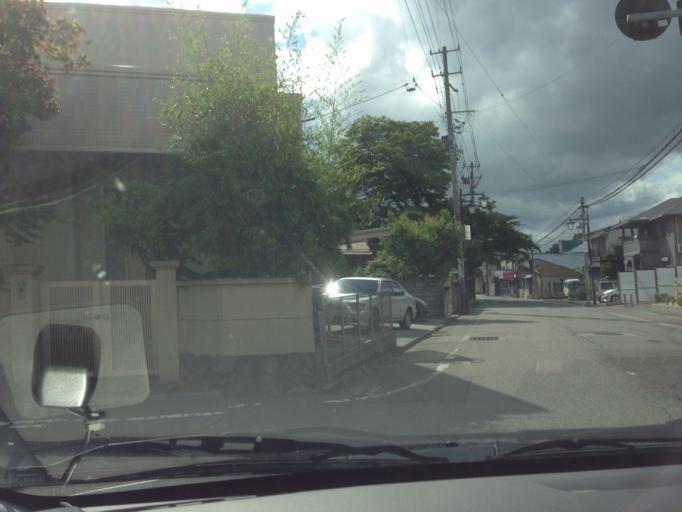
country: JP
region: Fukushima
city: Kitakata
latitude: 37.4943
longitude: 139.9341
